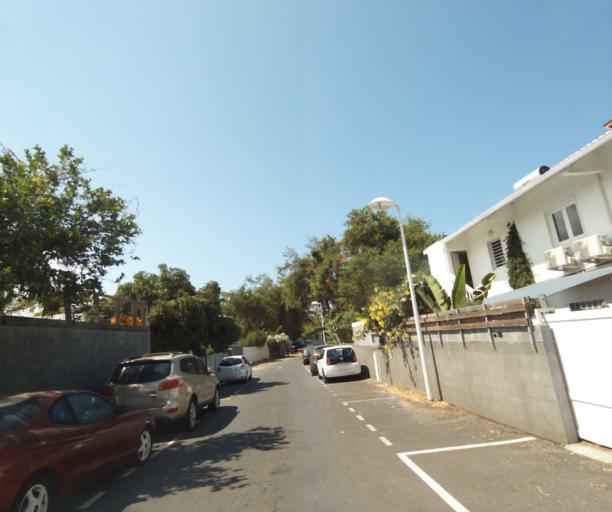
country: RE
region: Reunion
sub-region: Reunion
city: Trois-Bassins
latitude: -21.0934
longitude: 55.2391
